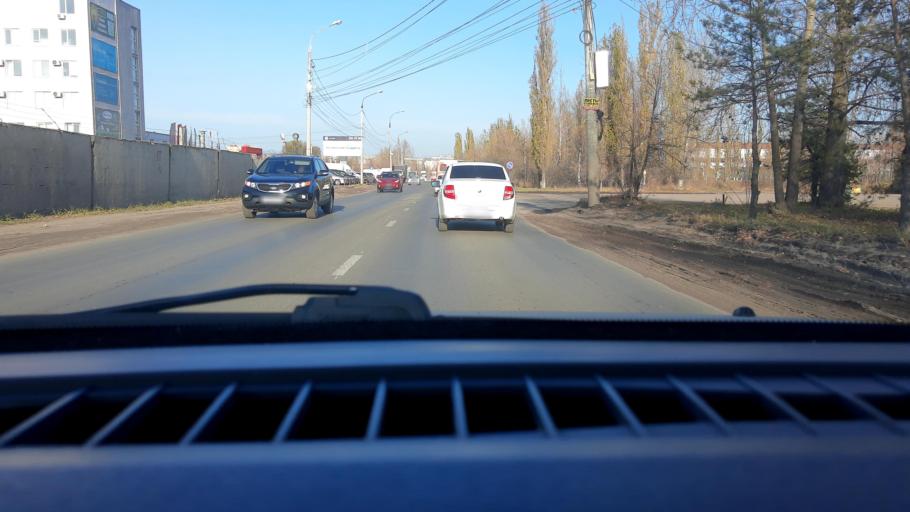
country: RU
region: Nizjnij Novgorod
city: Gorbatovka
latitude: 56.3525
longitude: 43.8020
